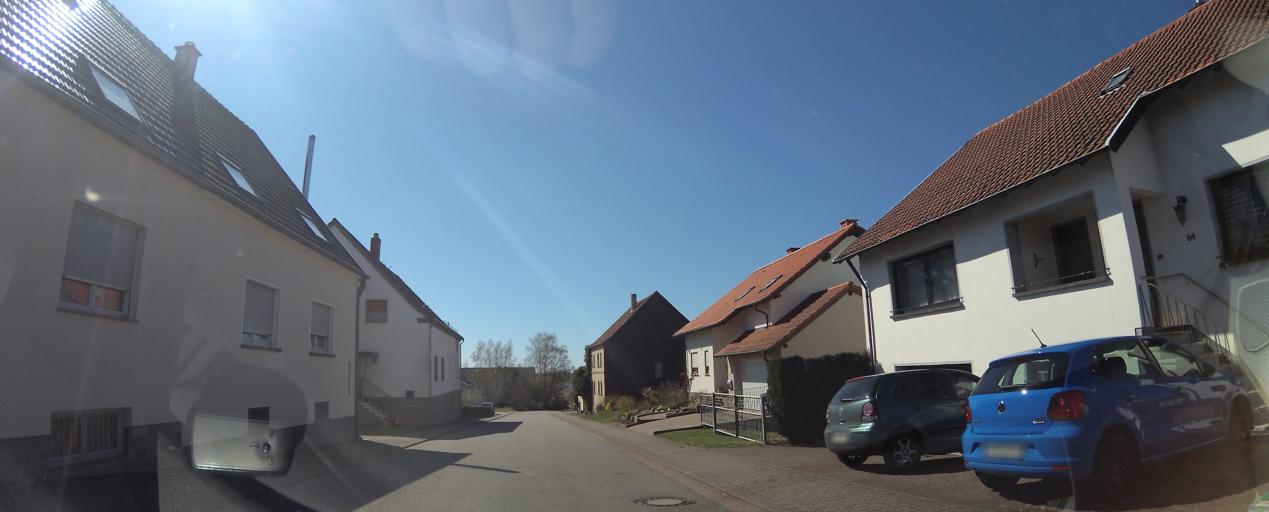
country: DE
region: Saarland
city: Heusweiler
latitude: 49.3479
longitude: 6.9747
